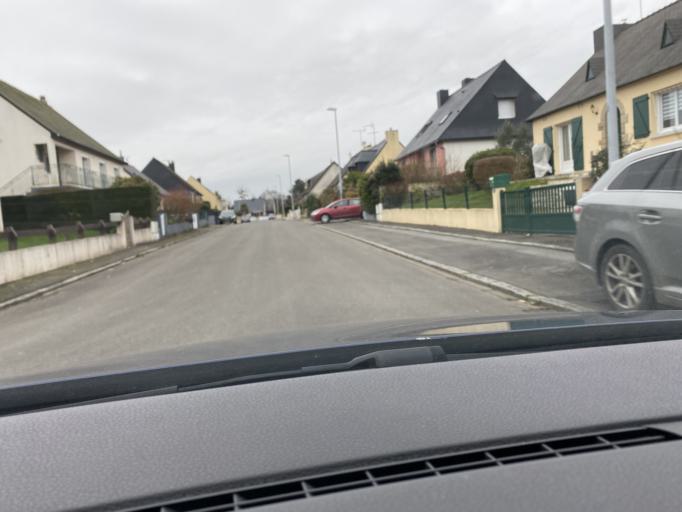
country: FR
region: Brittany
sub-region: Departement d'Ille-et-Vilaine
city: Melesse
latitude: 48.2205
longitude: -1.6900
